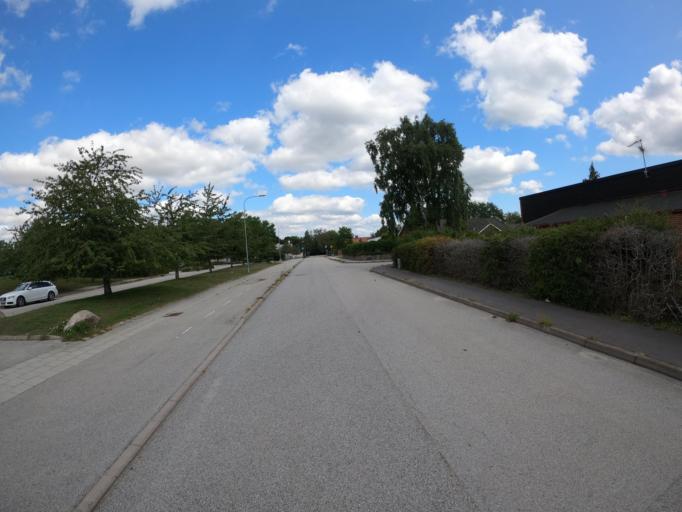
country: SE
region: Skane
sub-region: Lunds Kommun
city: Genarp
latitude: 55.5983
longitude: 13.3974
